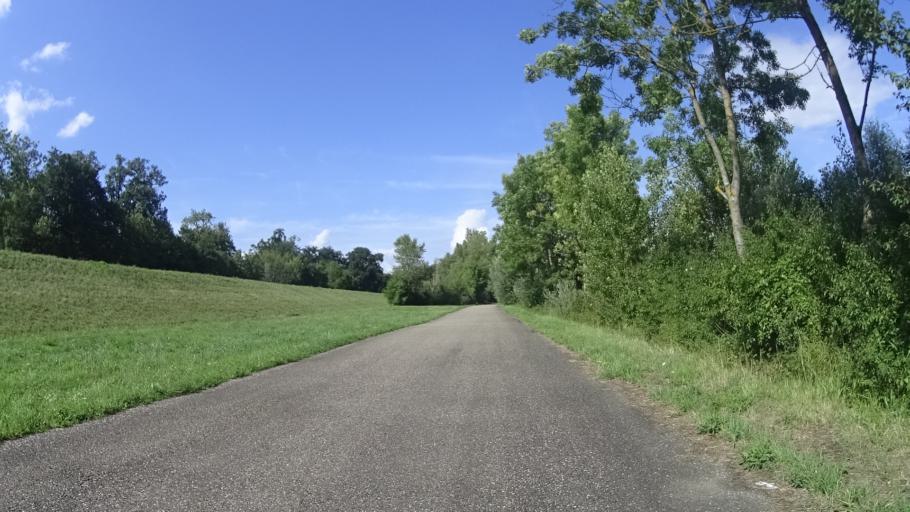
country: DE
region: Baden-Wuerttemberg
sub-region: Karlsruhe Region
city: Hugelsheim
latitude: 48.8366
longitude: 8.1025
